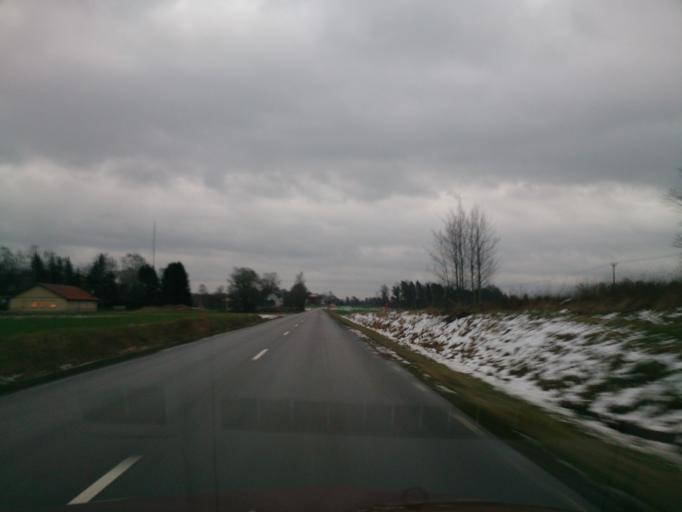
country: SE
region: OEstergoetland
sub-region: Norrkopings Kommun
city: Kimstad
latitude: 58.4115
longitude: 15.9194
